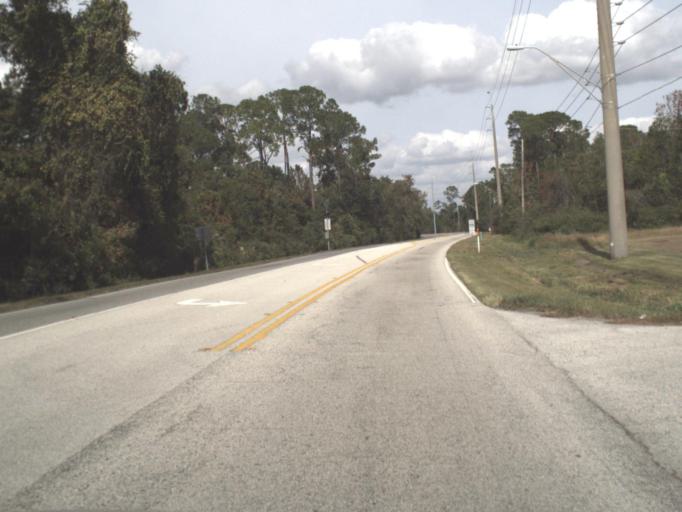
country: US
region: Florida
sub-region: Osceola County
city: Poinciana
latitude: 28.1632
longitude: -81.4466
